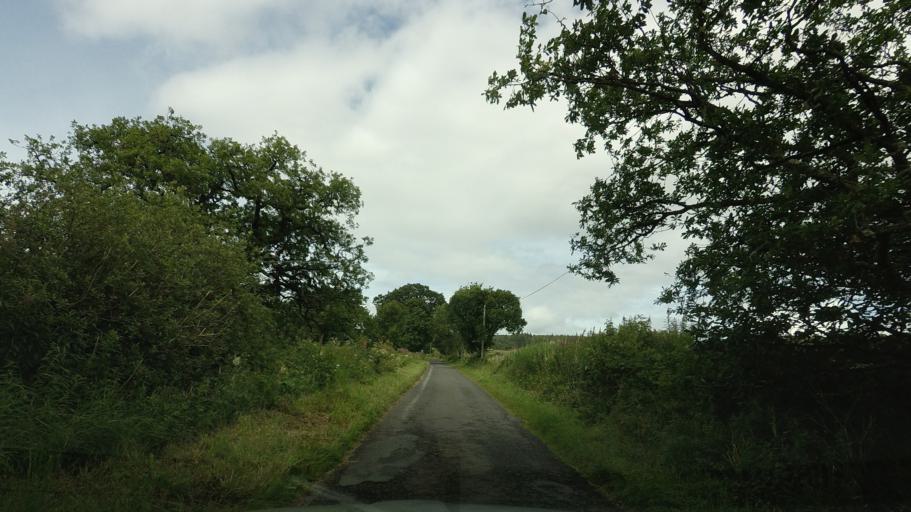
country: GB
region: Scotland
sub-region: Stirling
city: Killearn
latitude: 56.0748
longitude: -4.4502
